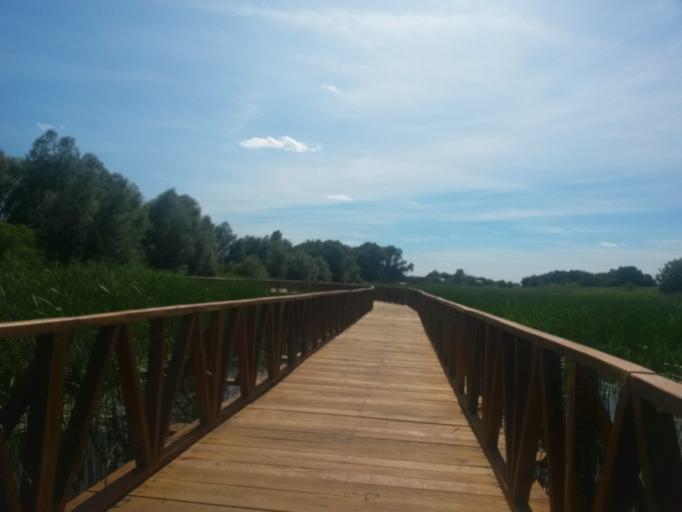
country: HR
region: Osjecko-Baranjska
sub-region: Grad Osijek
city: Bilje
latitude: 45.6085
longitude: 18.7944
